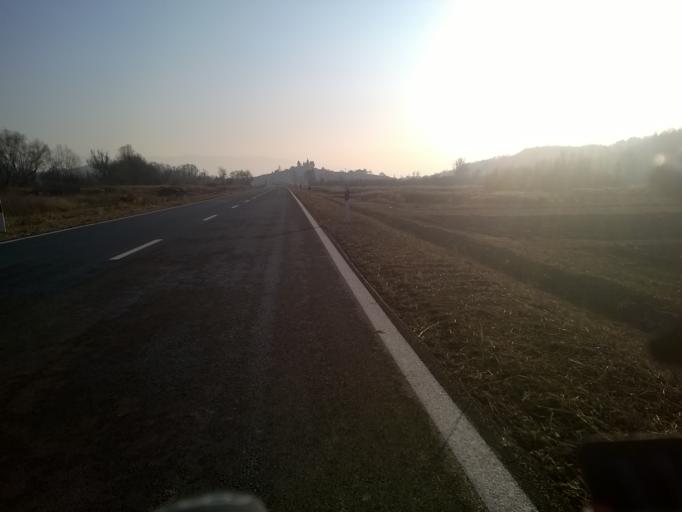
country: HR
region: Krapinsko-Zagorska
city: Zabok
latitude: 46.0508
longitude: 15.9132
